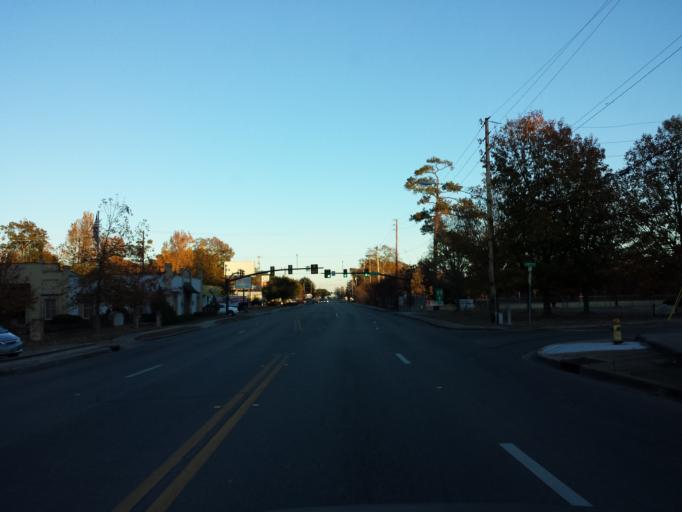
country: US
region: Mississippi
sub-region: Forrest County
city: Hattiesburg
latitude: 31.3247
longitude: -89.3188
